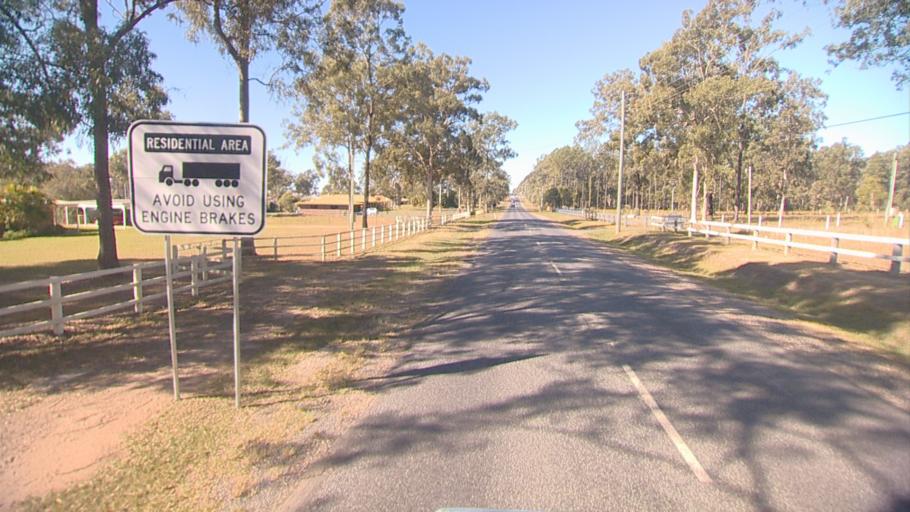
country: AU
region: Queensland
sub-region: Logan
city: Logan Reserve
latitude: -27.7123
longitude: 153.1034
